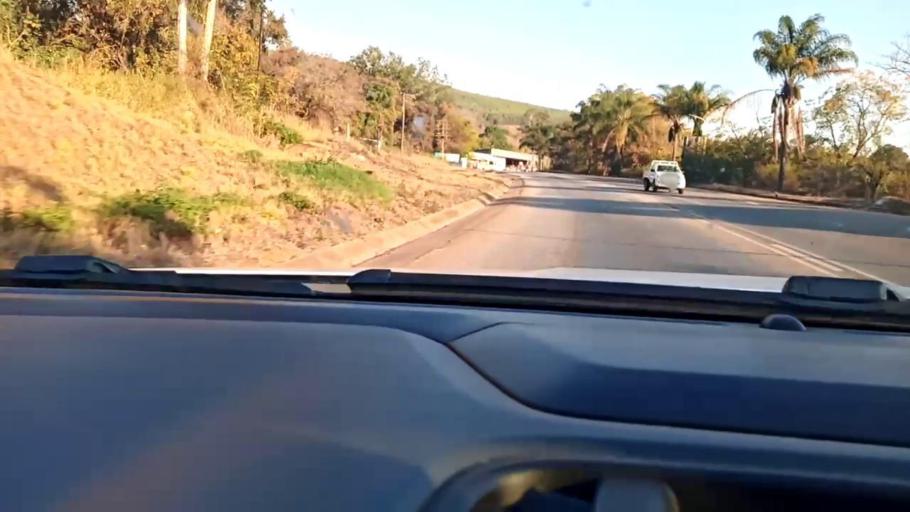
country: ZA
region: Limpopo
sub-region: Mopani District Municipality
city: Duiwelskloof
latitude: -23.6907
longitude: 30.1464
